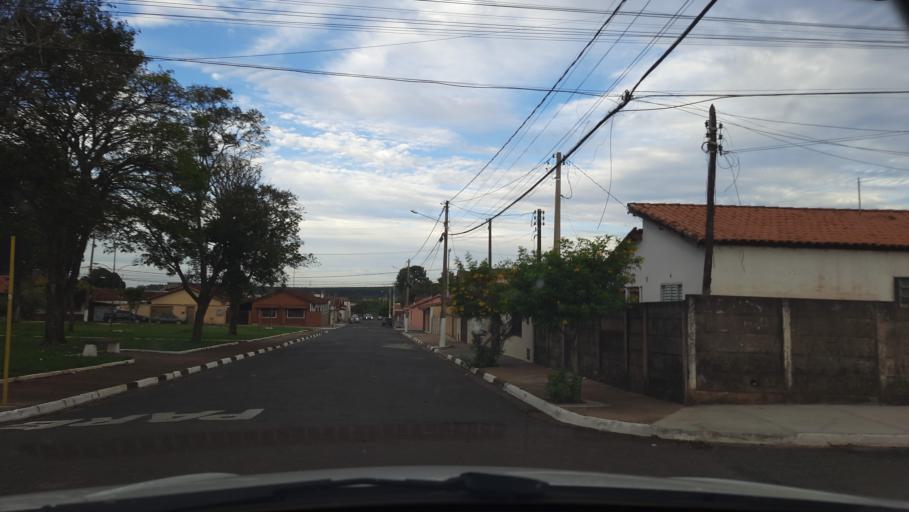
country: BR
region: Sao Paulo
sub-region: Casa Branca
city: Casa Branca
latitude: -21.7815
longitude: -47.0660
